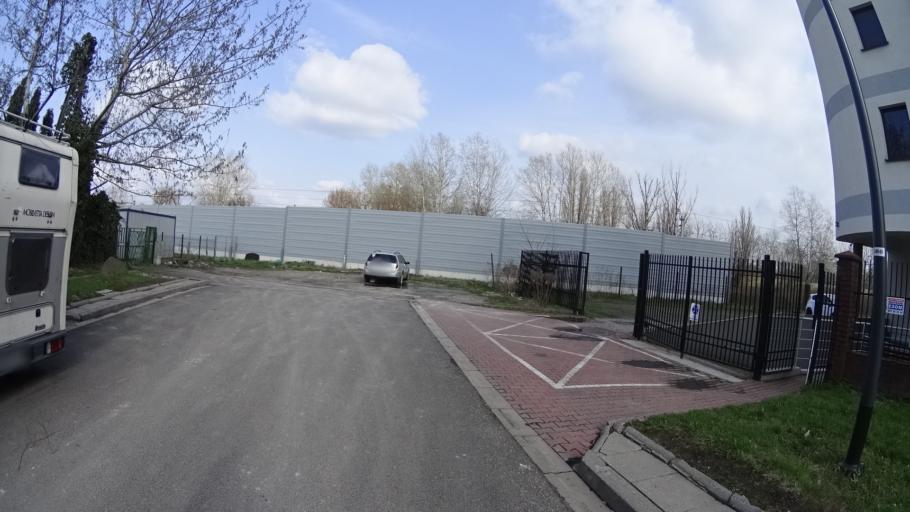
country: PL
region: Masovian Voivodeship
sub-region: Warszawa
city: Bemowo
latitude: 52.2299
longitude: 20.9211
